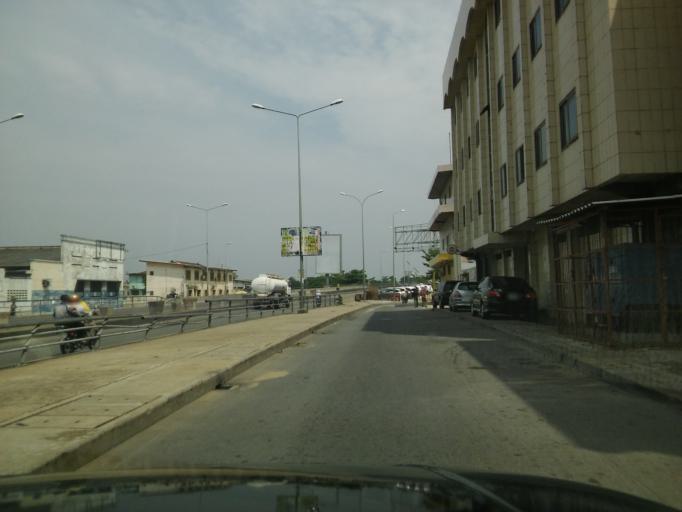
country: BJ
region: Littoral
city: Cotonou
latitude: 6.3584
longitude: 2.4389
